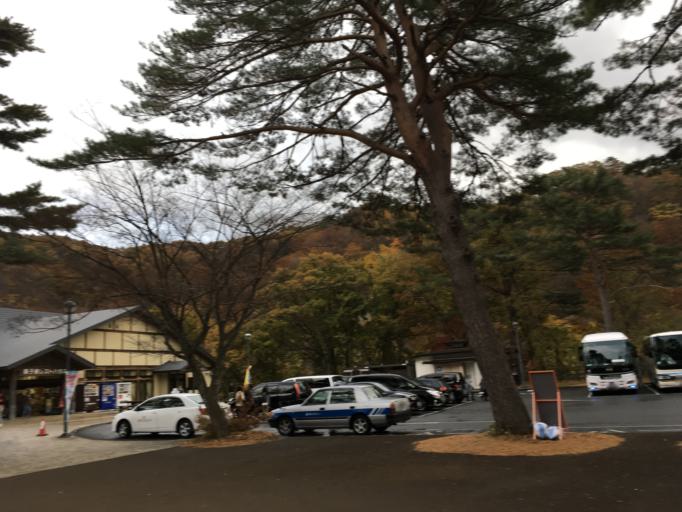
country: JP
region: Miyagi
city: Furukawa
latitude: 38.7289
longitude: 140.6903
